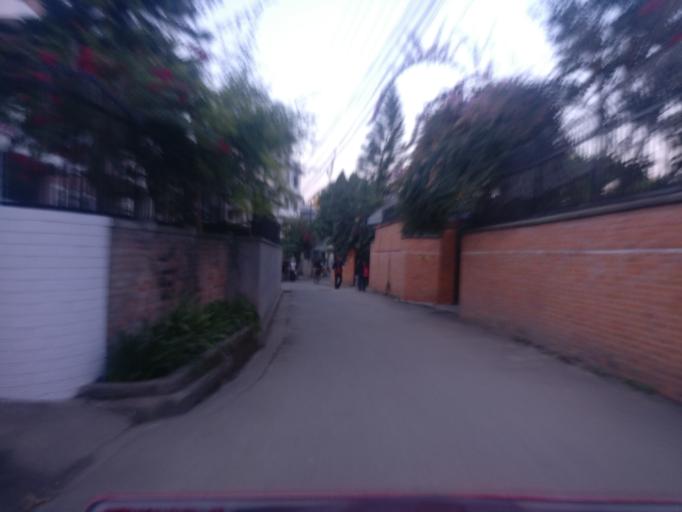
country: NP
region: Central Region
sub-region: Bagmati Zone
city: Patan
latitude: 27.6504
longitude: 85.3187
